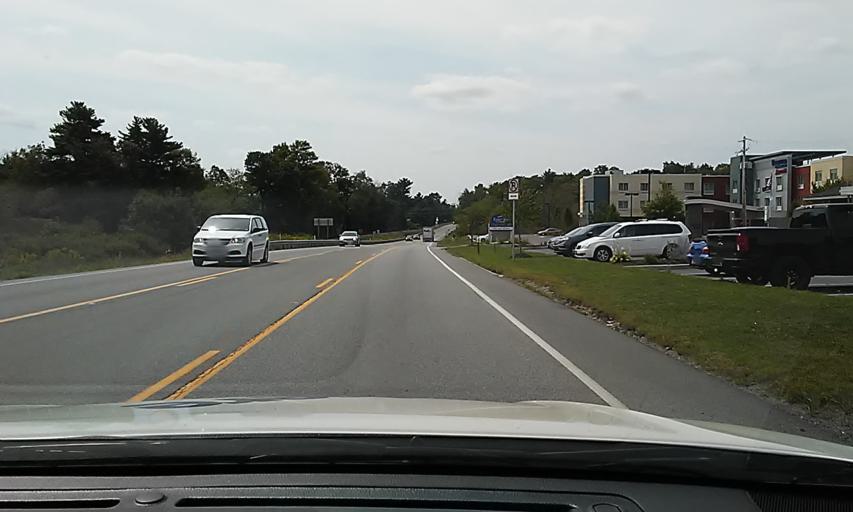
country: US
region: Pennsylvania
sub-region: Clearfield County
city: Treasure Lake
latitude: 41.1272
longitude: -78.7121
